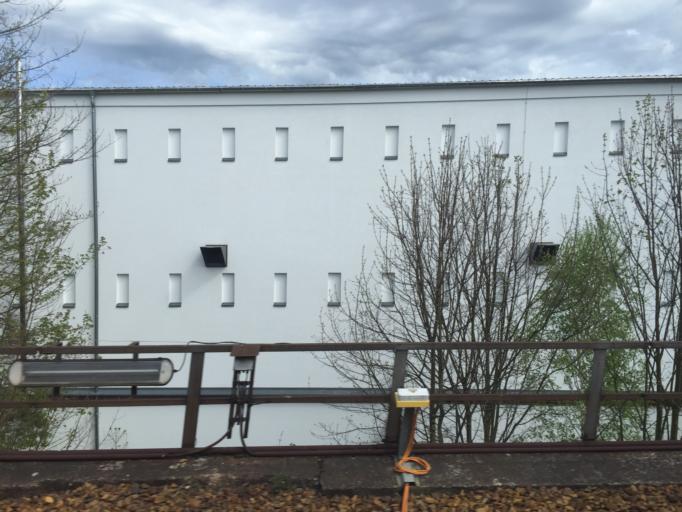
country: DE
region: Saxony
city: Lobau
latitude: 51.0986
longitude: 14.6763
